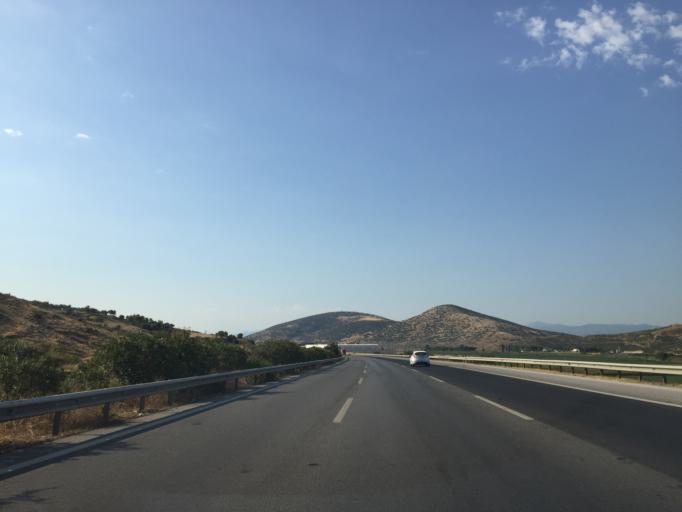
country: TR
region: Izmir
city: Belevi
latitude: 38.0436
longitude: 27.4288
